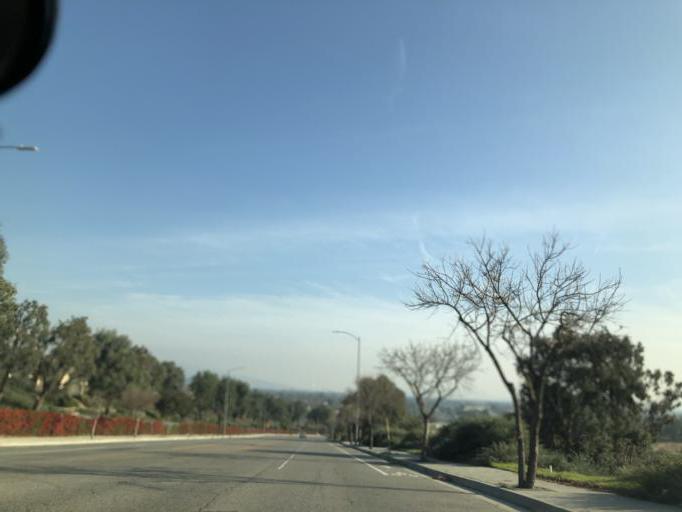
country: US
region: California
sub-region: Los Angeles County
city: San Fernando
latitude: 34.2873
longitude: -118.4616
